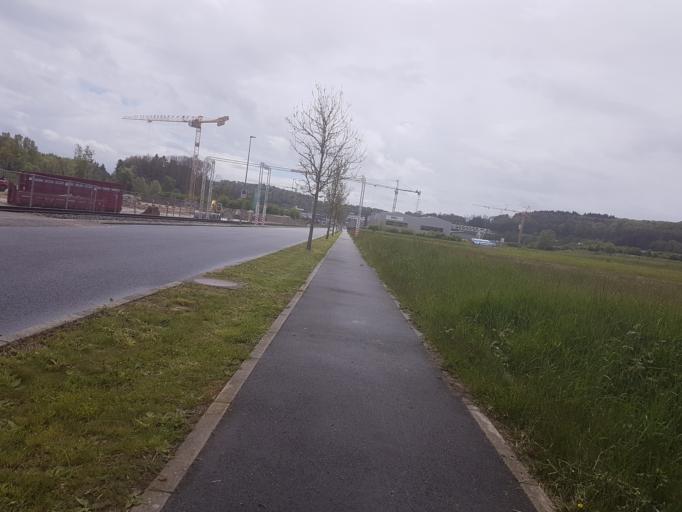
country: CH
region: Vaud
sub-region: Ouest Lausannois District
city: Bussigny
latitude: 46.5722
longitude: 6.5282
